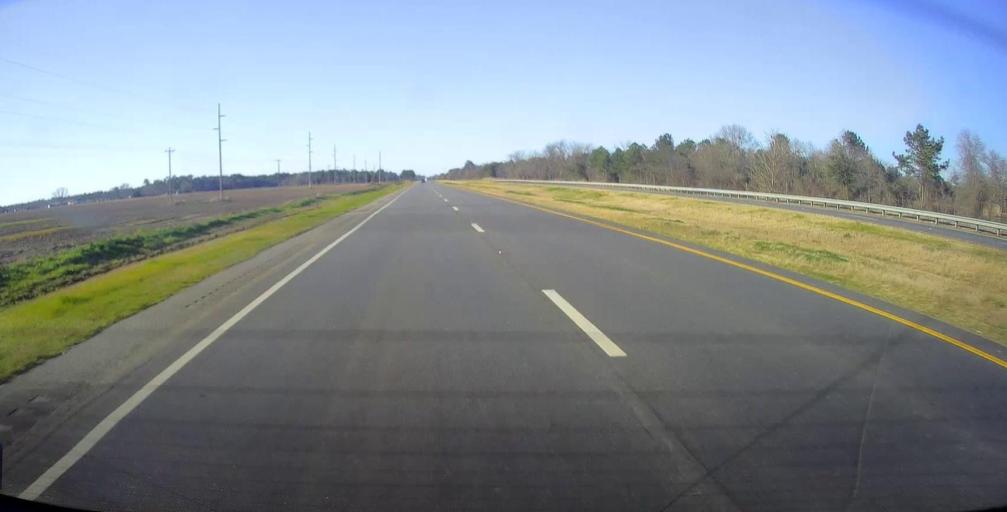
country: US
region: Georgia
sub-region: Lee County
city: Leesburg
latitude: 31.7931
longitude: -84.2012
